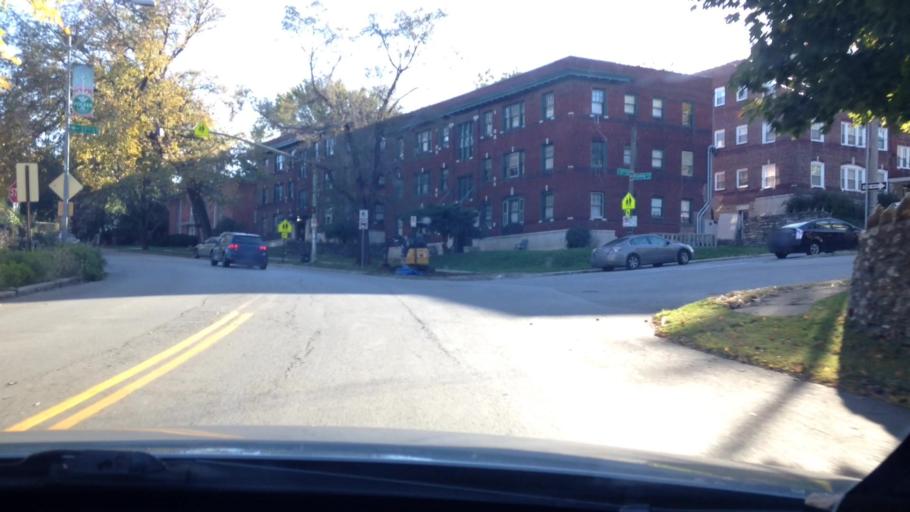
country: US
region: Kansas
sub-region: Johnson County
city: Westwood
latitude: 39.0608
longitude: -94.6035
